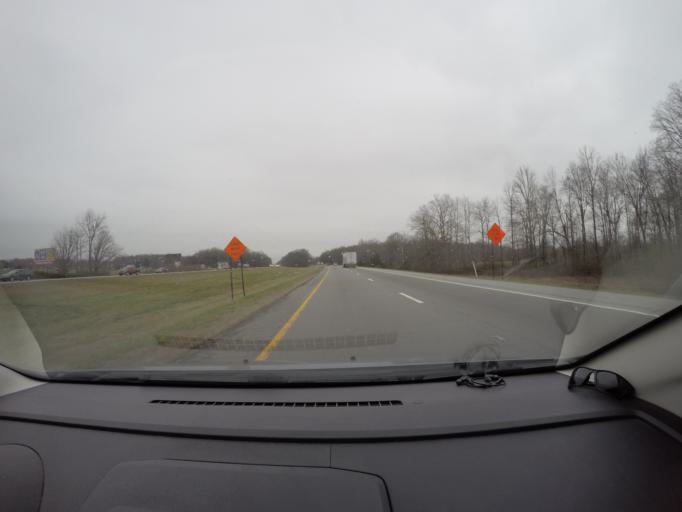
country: US
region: Tennessee
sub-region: Coffee County
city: Manchester
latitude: 35.4491
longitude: -86.0478
